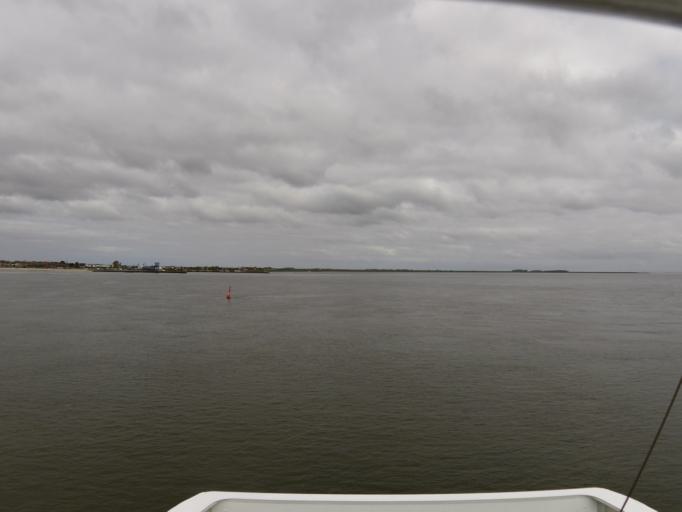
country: DE
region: Schleswig-Holstein
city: Wyk auf Fohr
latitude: 54.6869
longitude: 8.5868
